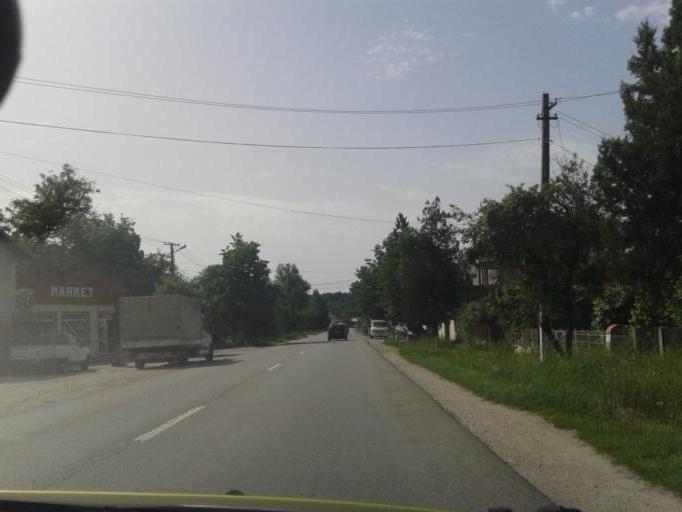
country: RO
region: Valcea
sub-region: Comuna Pietrari
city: Pietrari
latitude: 45.1052
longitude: 24.1200
